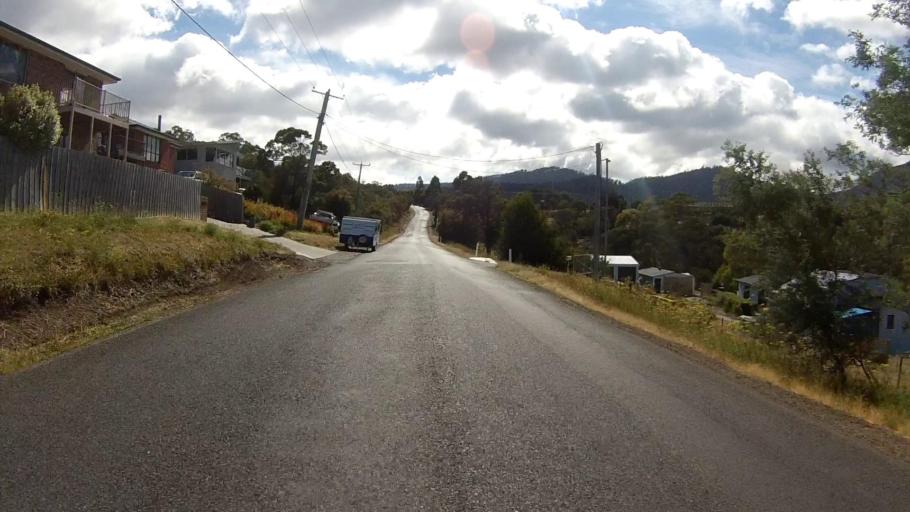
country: AU
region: Tasmania
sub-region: Brighton
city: Old Beach
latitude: -42.7761
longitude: 147.2835
